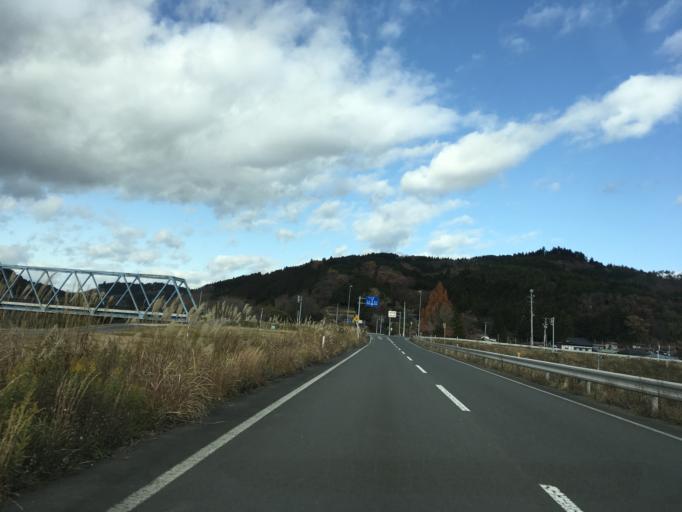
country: JP
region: Iwate
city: Ichinoseki
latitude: 38.8426
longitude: 141.2646
